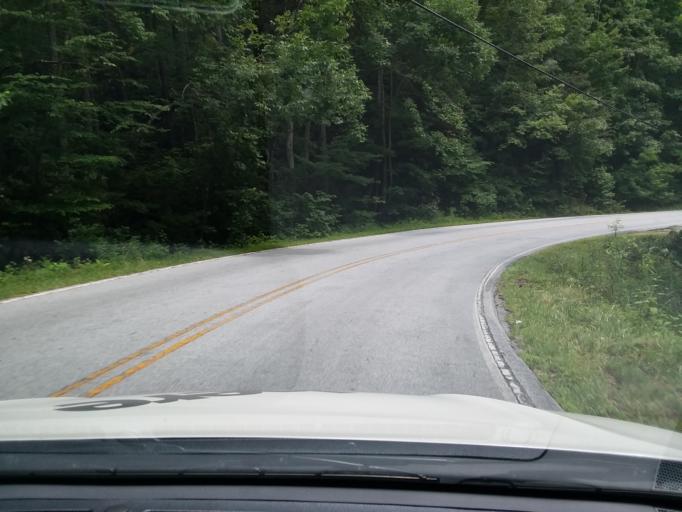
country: US
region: Georgia
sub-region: Rabun County
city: Mountain City
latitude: 35.0316
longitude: -83.1966
